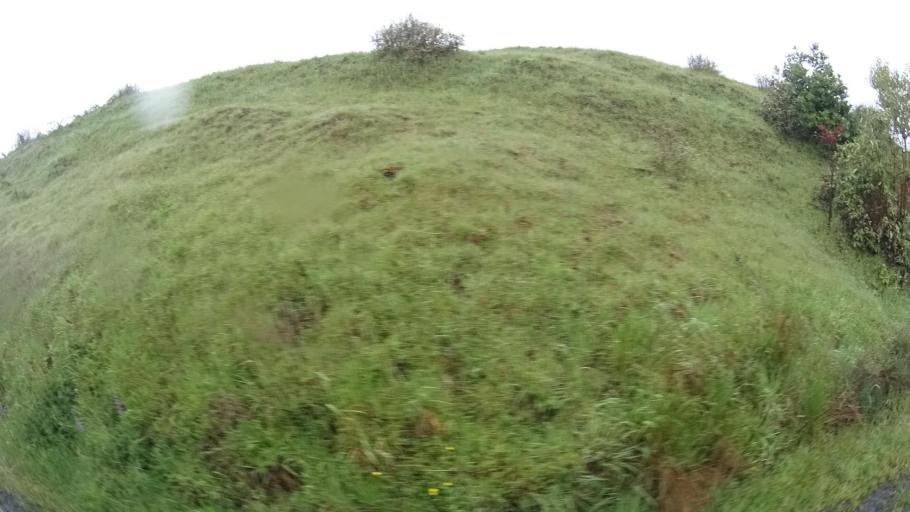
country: US
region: California
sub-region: Humboldt County
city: Westhaven-Moonstone
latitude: 41.1679
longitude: -123.9171
